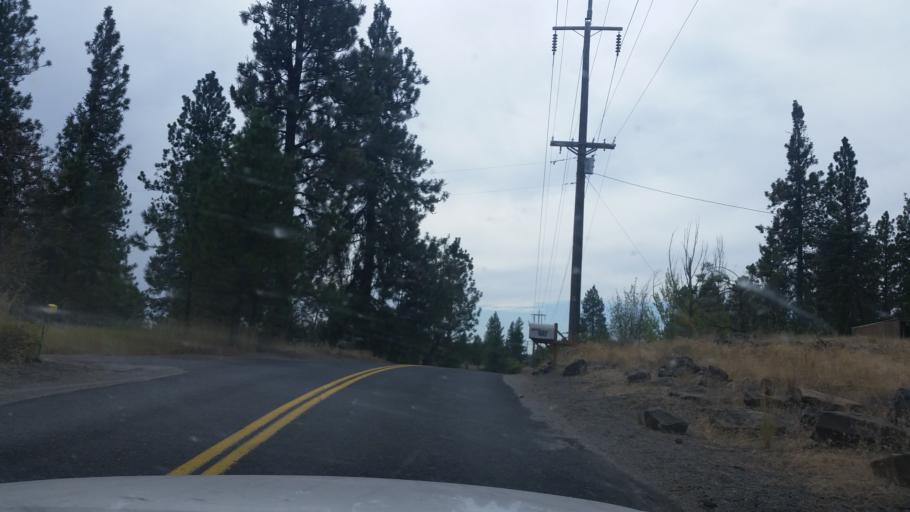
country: US
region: Washington
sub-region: Spokane County
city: Spokane
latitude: 47.6457
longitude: -117.4969
